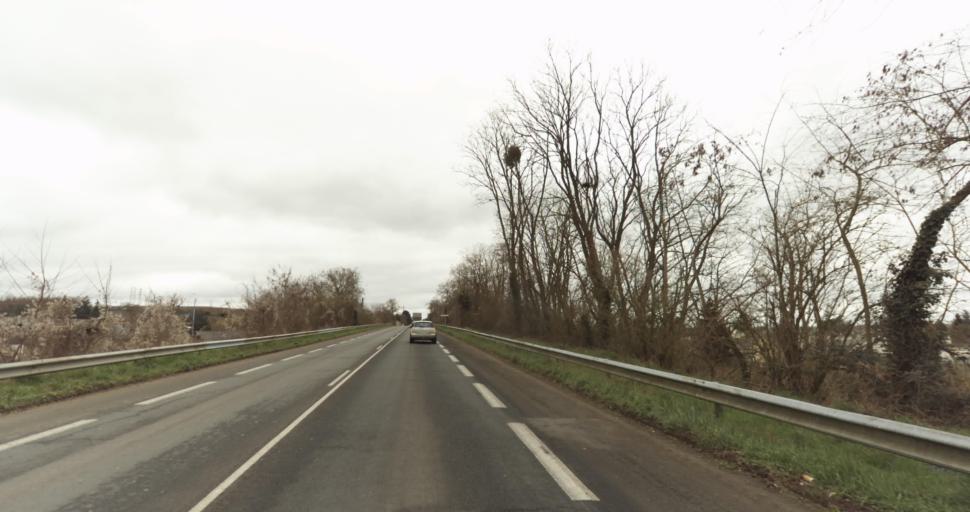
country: FR
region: Pays de la Loire
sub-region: Departement de Maine-et-Loire
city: Varrains
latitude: 47.2355
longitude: -0.0760
